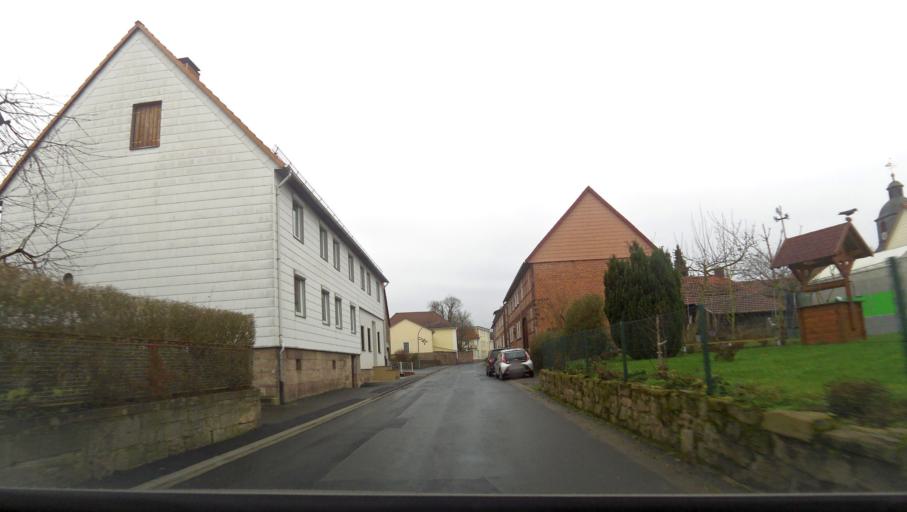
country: DE
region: Lower Saxony
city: Buhren
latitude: 51.4947
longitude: 9.6048
